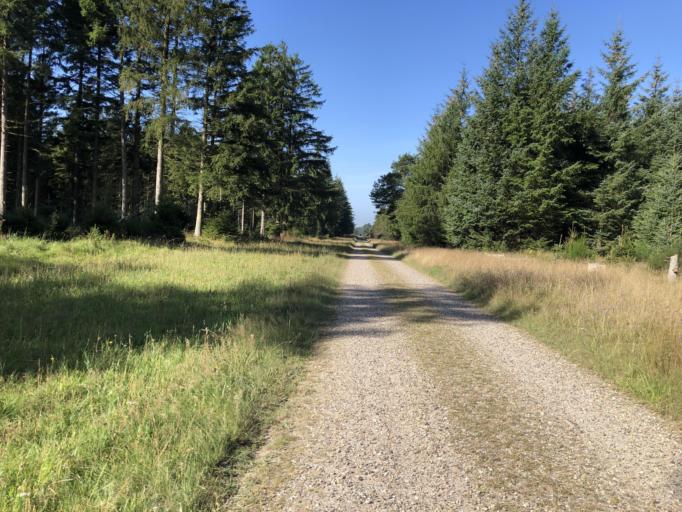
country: DK
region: Central Jutland
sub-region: Lemvig Kommune
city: Lemvig
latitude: 56.4773
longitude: 8.3252
